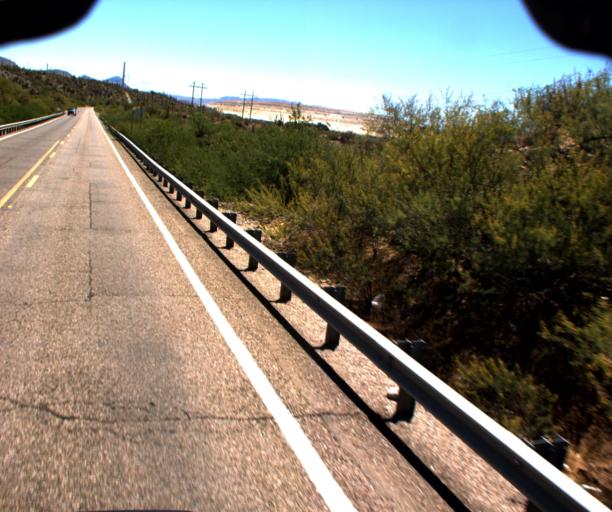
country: US
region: Arizona
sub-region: Pinal County
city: Kearny
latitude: 33.0148
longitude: -110.8339
